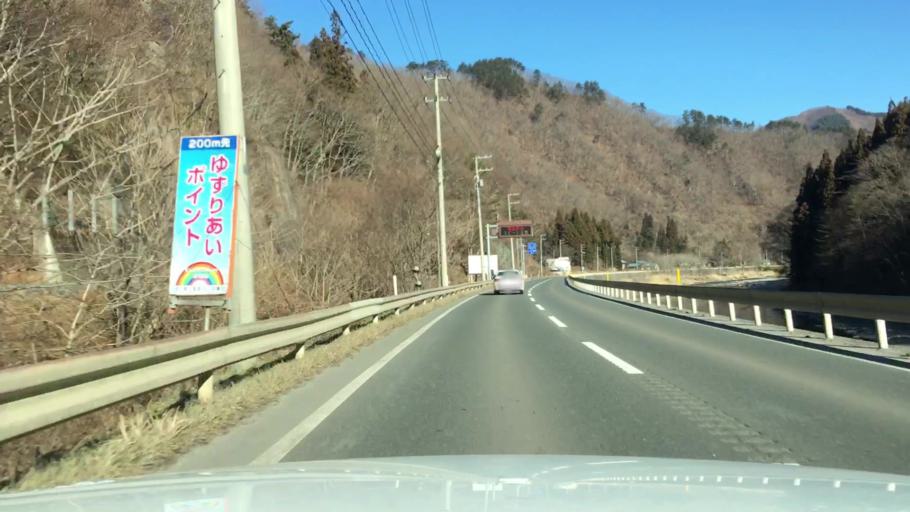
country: JP
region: Iwate
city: Miyako
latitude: 39.6115
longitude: 141.7881
